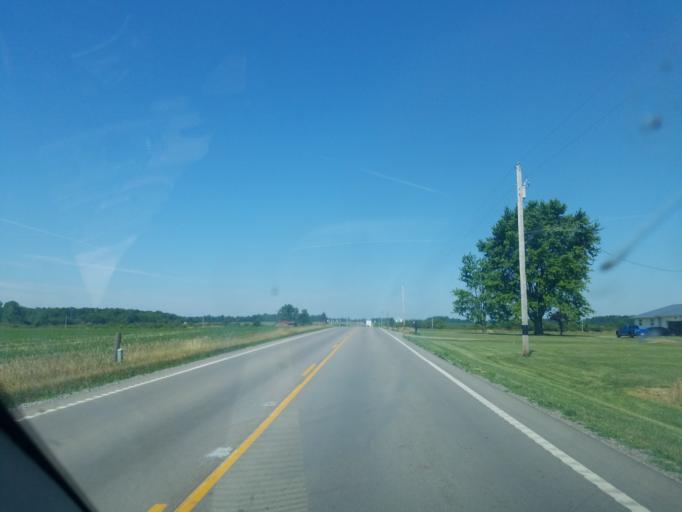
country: US
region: Ohio
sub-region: Shelby County
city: Jackson Center
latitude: 40.4393
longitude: -83.9903
